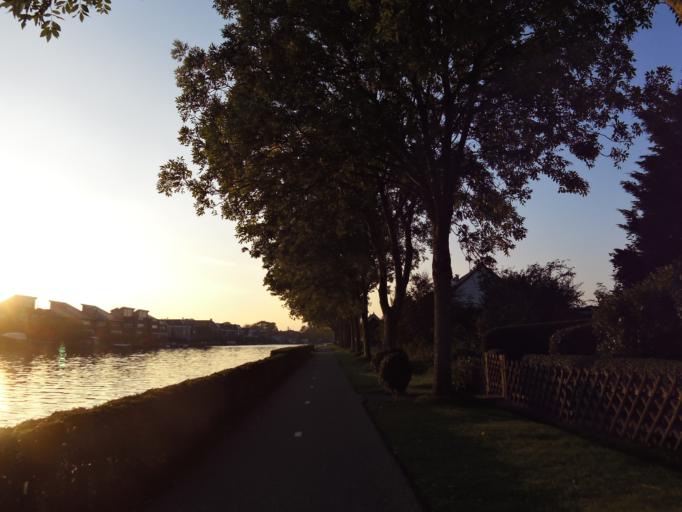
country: NL
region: South Holland
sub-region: Gemeente Leiderdorp
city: Leiderdorp
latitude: 52.1297
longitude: 4.5672
